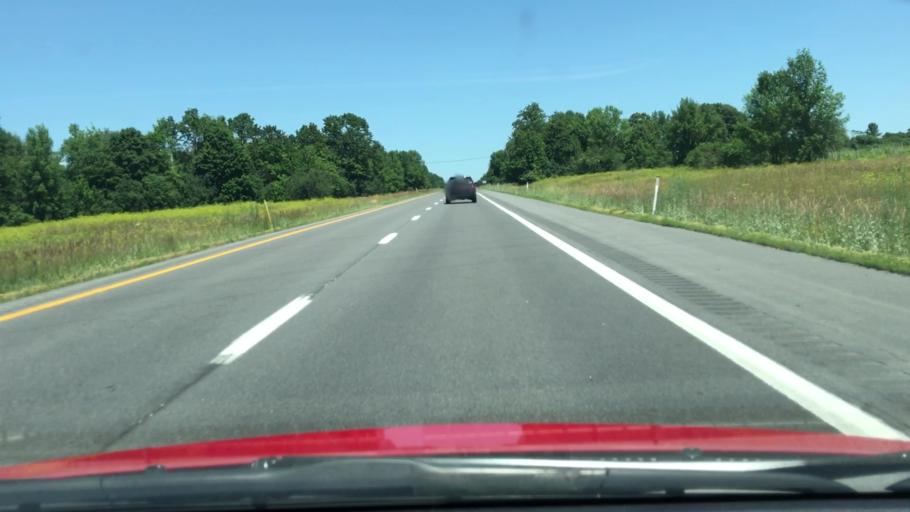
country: US
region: New York
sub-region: Clinton County
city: Cumberland Head
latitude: 44.7350
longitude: -73.4350
